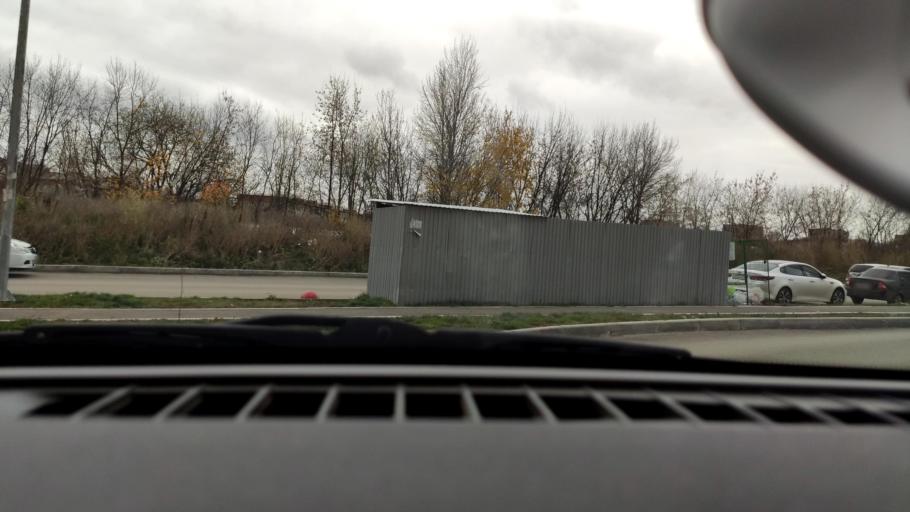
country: RU
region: Perm
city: Perm
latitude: 57.9906
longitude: 56.2704
